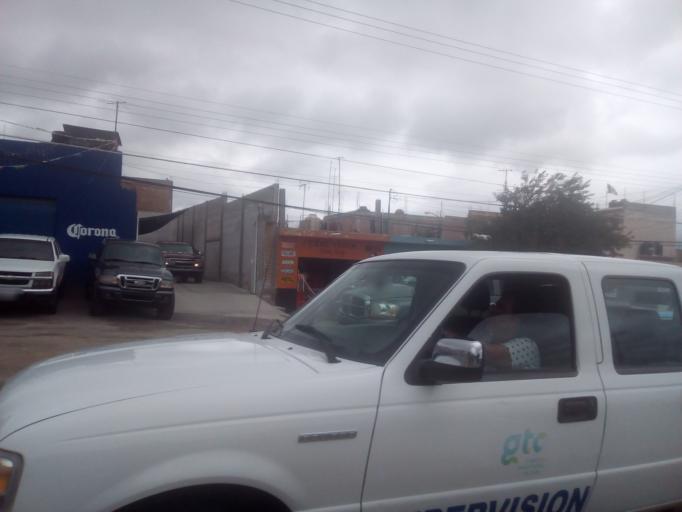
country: MX
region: Guerrero
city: San Luis de la Paz
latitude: 21.2886
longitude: -100.5132
